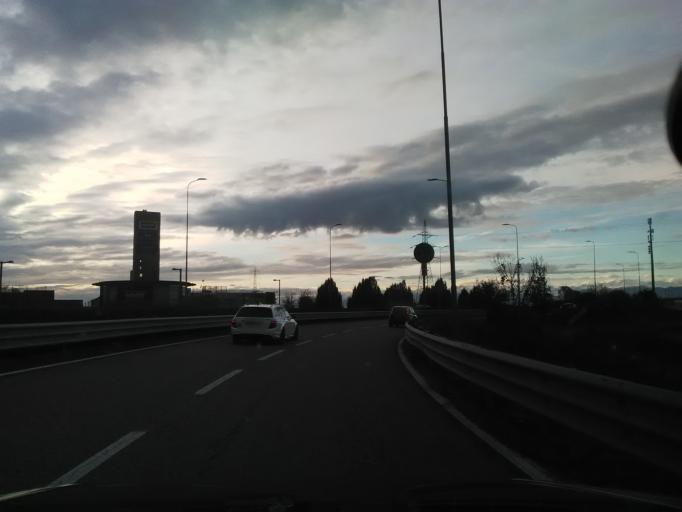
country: IT
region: Piedmont
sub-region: Provincia di Novara
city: Vicolungo
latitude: 45.4696
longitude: 8.4596
